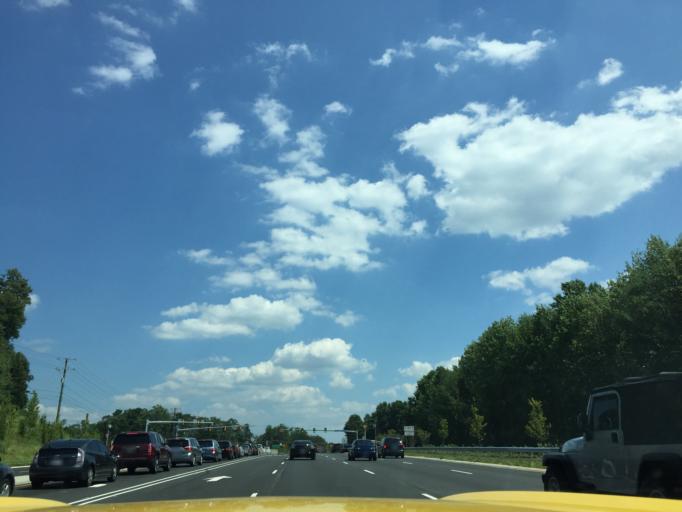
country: US
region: Virginia
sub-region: Fairfax County
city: Dranesville
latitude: 39.0014
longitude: -77.3471
